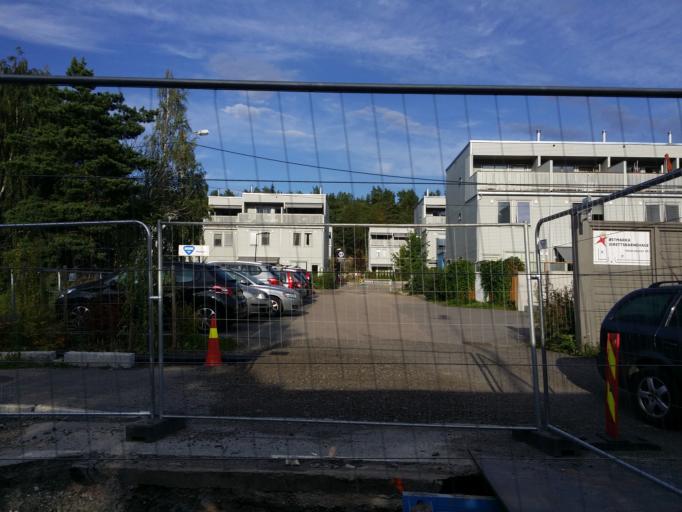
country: NO
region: Akershus
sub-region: Oppegard
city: Kolbotn
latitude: 59.8992
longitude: 10.8519
